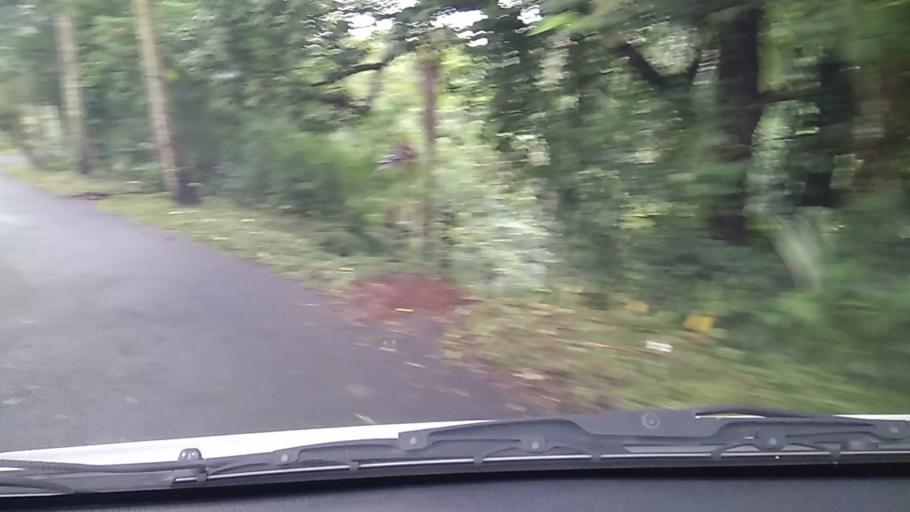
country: ID
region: Bali
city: Banjar Dujung Kaja
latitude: -8.4051
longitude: 115.2890
